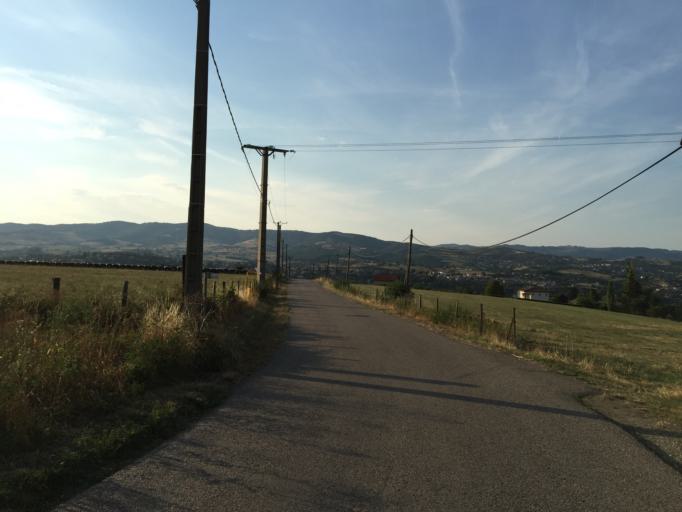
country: FR
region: Rhone-Alpes
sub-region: Departement de la Loire
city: Saint-Paul-en-Jarez
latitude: 45.4782
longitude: 4.5504
